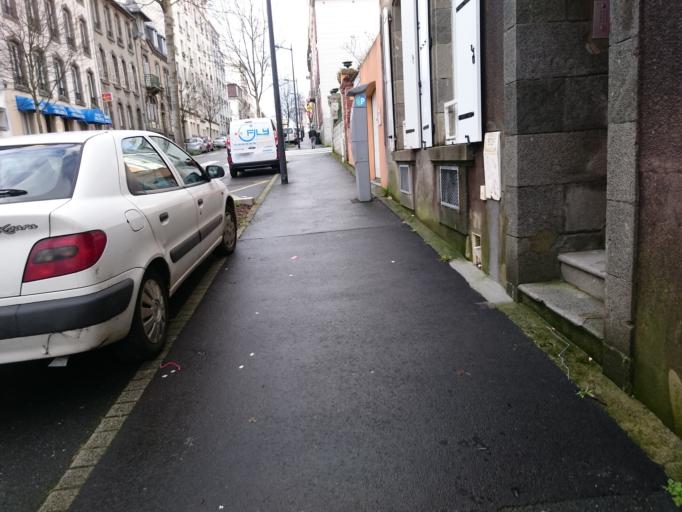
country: FR
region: Brittany
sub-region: Departement du Finistere
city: Brest
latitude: 48.3904
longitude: -4.4777
